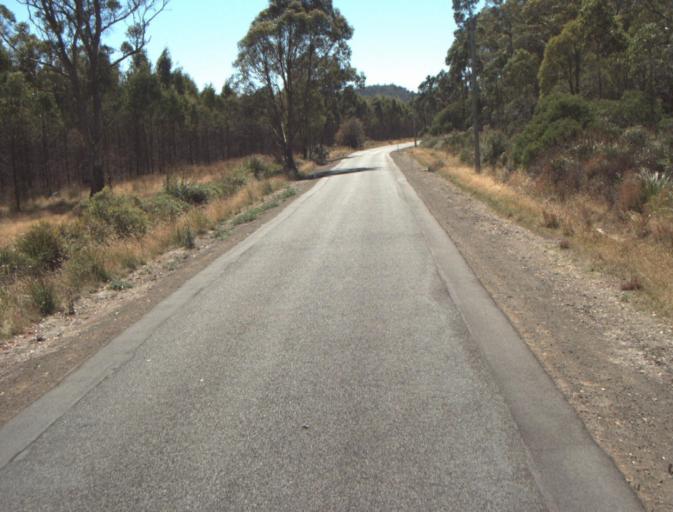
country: AU
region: Tasmania
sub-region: Launceston
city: Newstead
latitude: -41.3274
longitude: 147.3132
